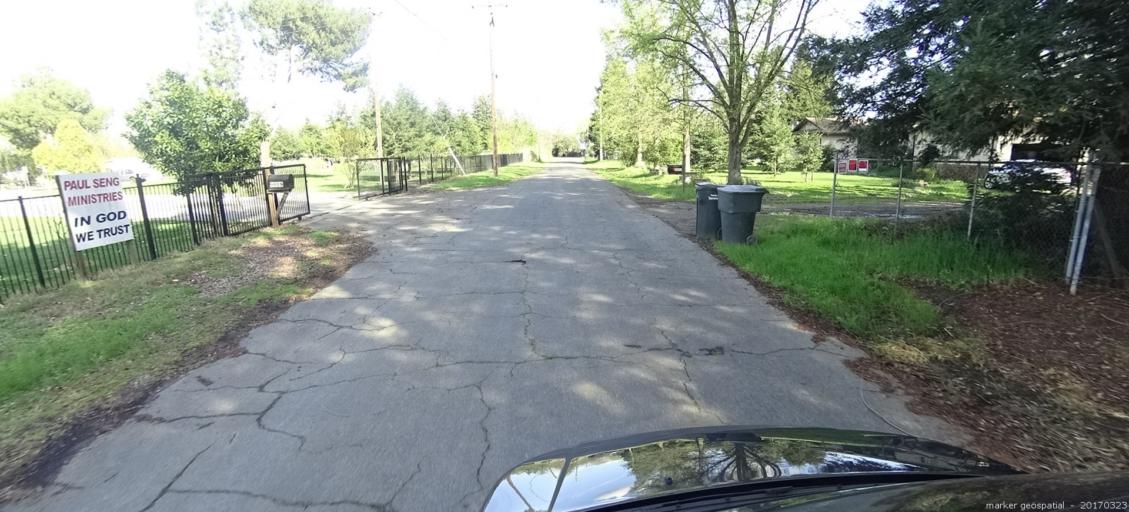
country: US
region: California
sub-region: Sacramento County
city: Rosemont
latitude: 38.5192
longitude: -121.3674
